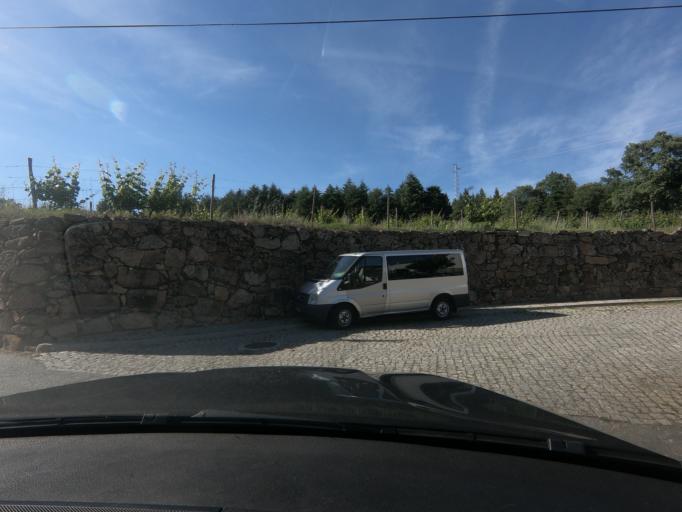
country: PT
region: Vila Real
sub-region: Vila Real
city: Vila Real
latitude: 41.2978
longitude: -7.7102
